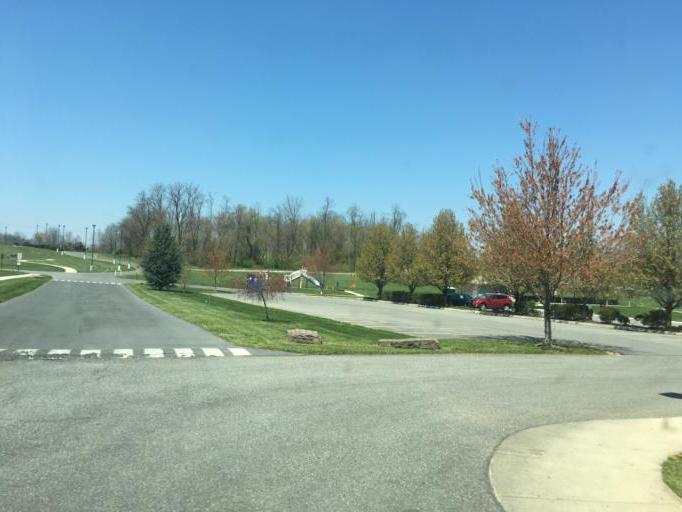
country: US
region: Maryland
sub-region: Washington County
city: Smithsburg
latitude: 39.6533
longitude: -77.5781
